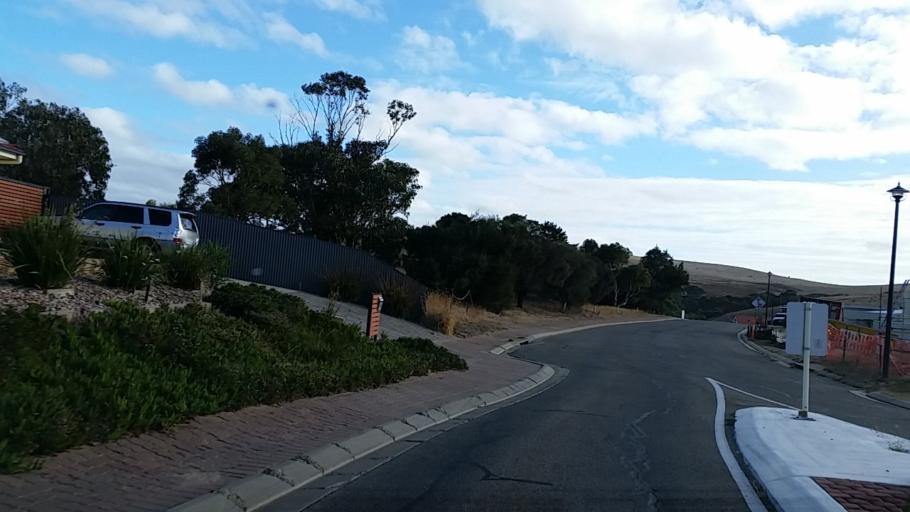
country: AU
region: South Australia
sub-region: Yankalilla
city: Normanville
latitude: -35.5041
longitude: 138.2475
